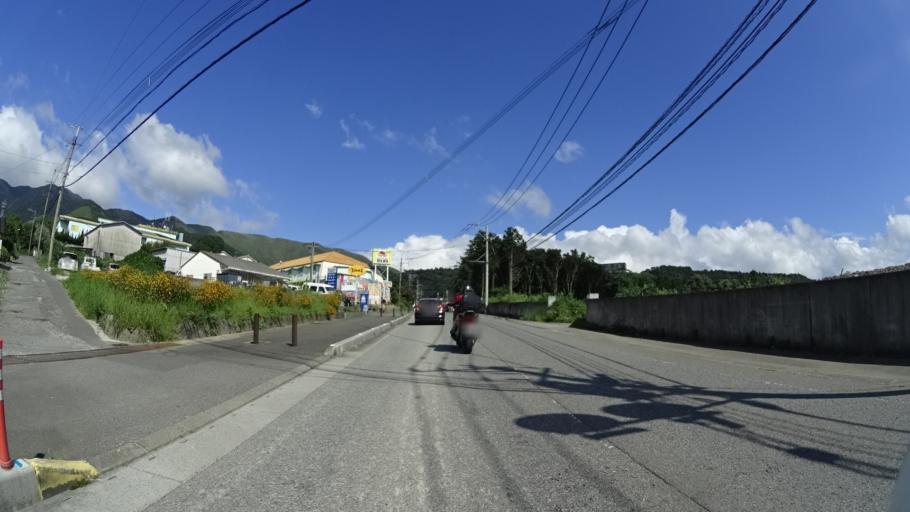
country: JP
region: Oita
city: Beppu
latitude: 33.3108
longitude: 131.4612
